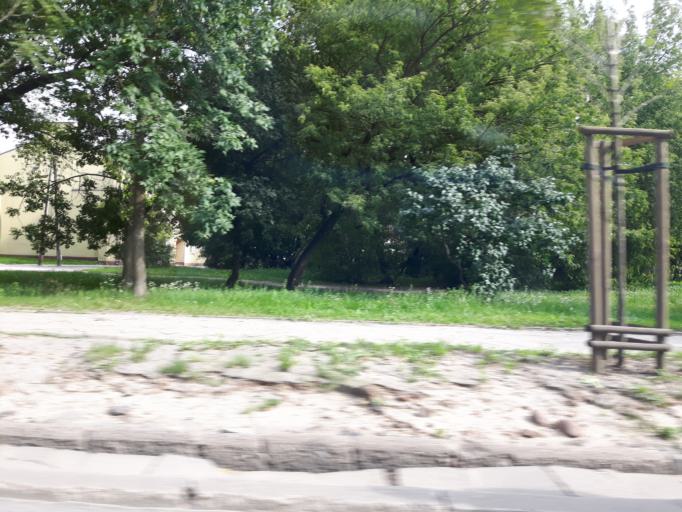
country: PL
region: Masovian Voivodeship
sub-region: Warszawa
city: Praga Poludnie
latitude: 52.2662
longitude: 21.0694
